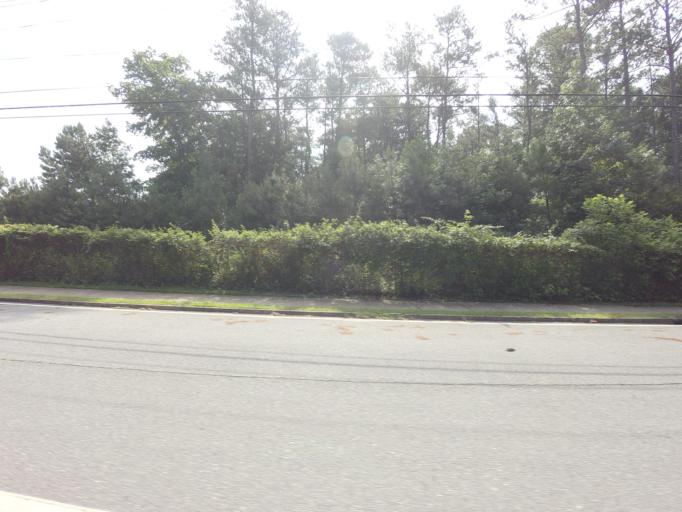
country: US
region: Georgia
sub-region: Fulton County
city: Johns Creek
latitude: 34.0352
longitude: -84.2348
